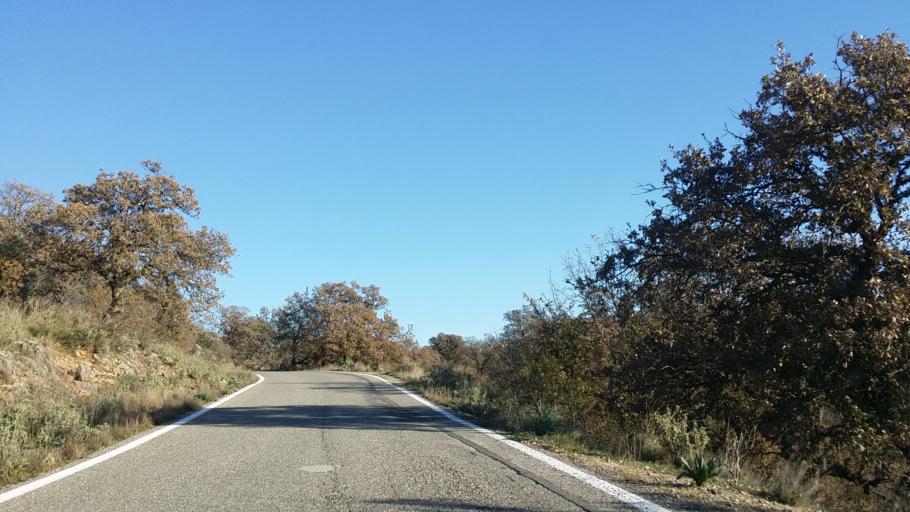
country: GR
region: West Greece
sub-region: Nomos Aitolias kai Akarnanias
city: Fitiai
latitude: 38.6354
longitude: 21.1937
